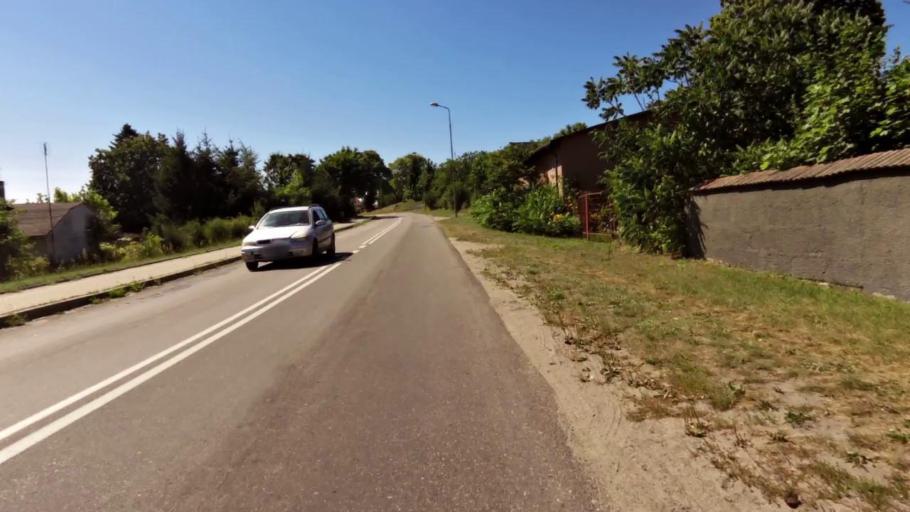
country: PL
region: West Pomeranian Voivodeship
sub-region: Powiat szczecinecki
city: Szczecinek
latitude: 53.7184
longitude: 16.6387
